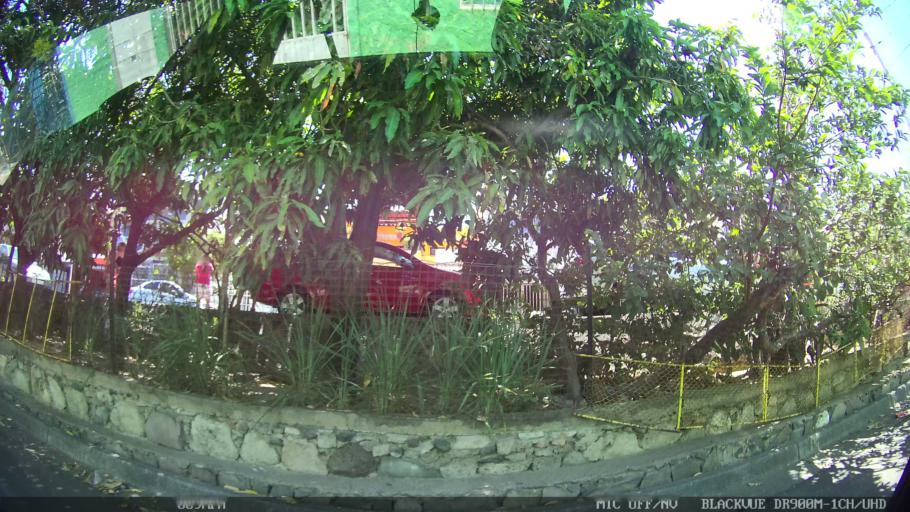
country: MX
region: Jalisco
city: Tlaquepaque
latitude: 20.6841
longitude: -103.2816
